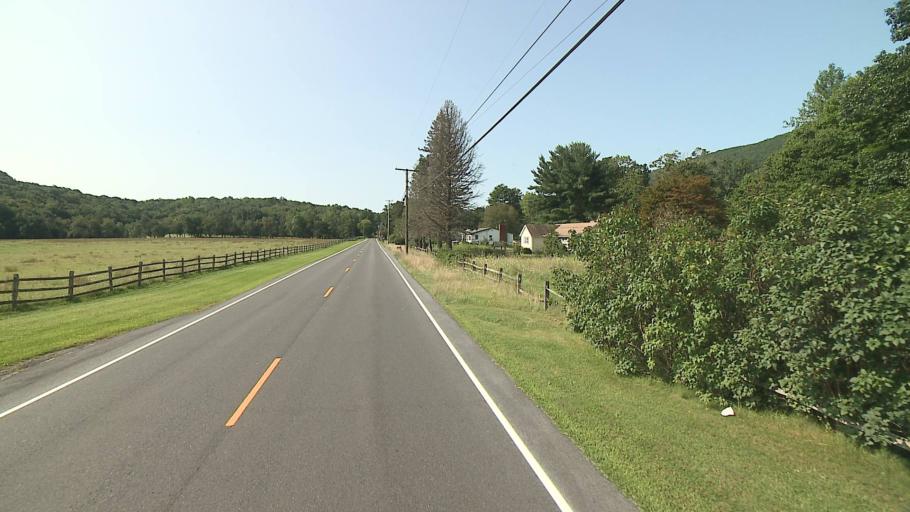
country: US
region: Connecticut
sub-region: Litchfield County
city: Kent
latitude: 41.7055
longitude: -73.4900
